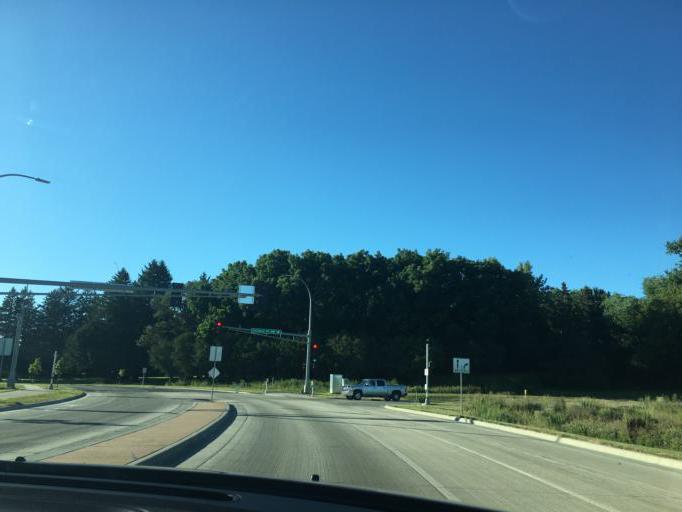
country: US
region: Minnesota
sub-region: Olmsted County
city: Rochester
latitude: 44.0788
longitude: -92.5235
